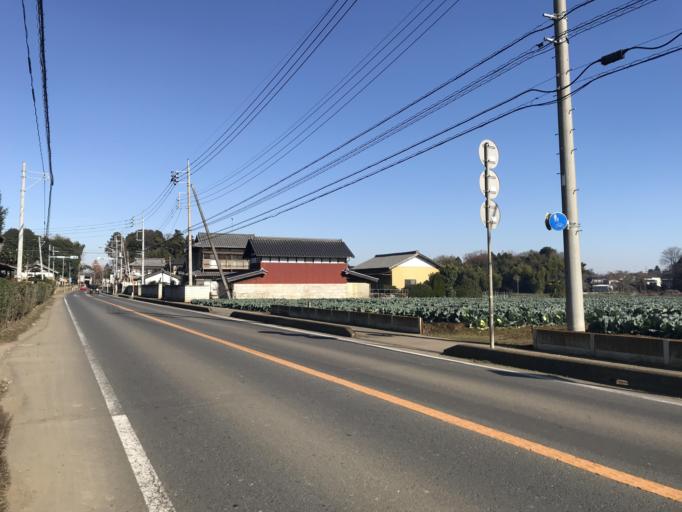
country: JP
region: Tochigi
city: Oyama
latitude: 36.2233
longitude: 139.8239
